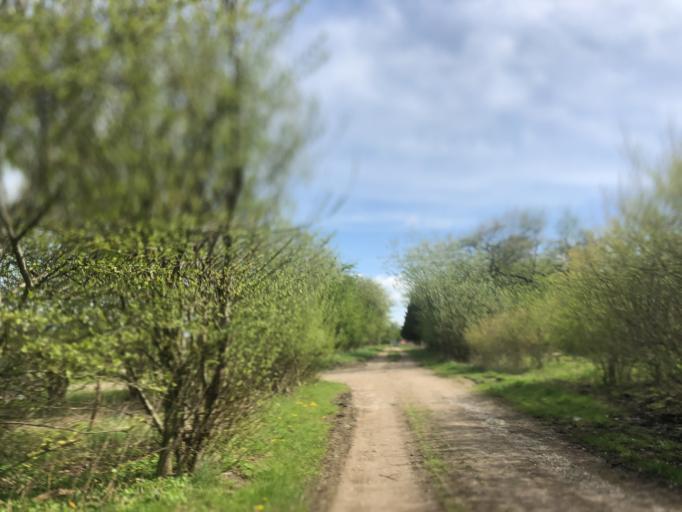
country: DK
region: Zealand
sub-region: Ringsted Kommune
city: Ringsted
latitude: 55.4520
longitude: 11.8138
